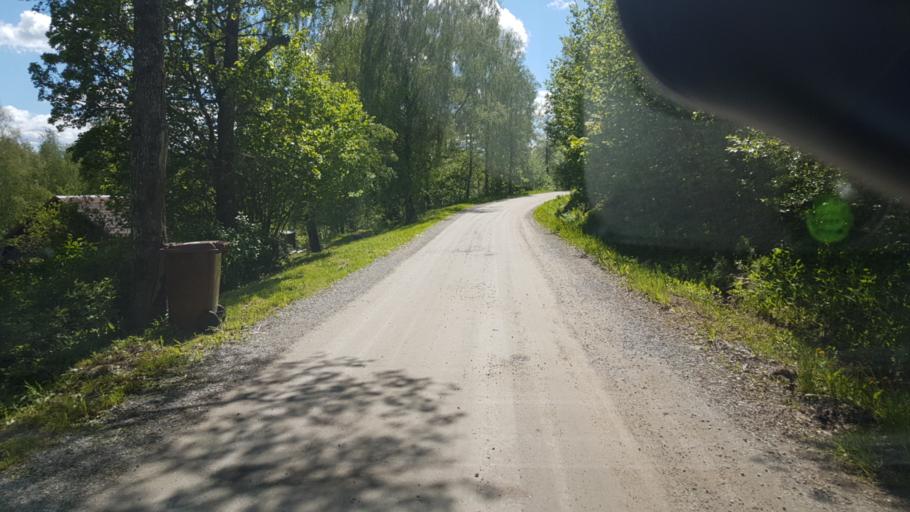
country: SE
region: Vaermland
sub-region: Sunne Kommun
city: Sunne
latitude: 59.7010
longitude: 12.8857
